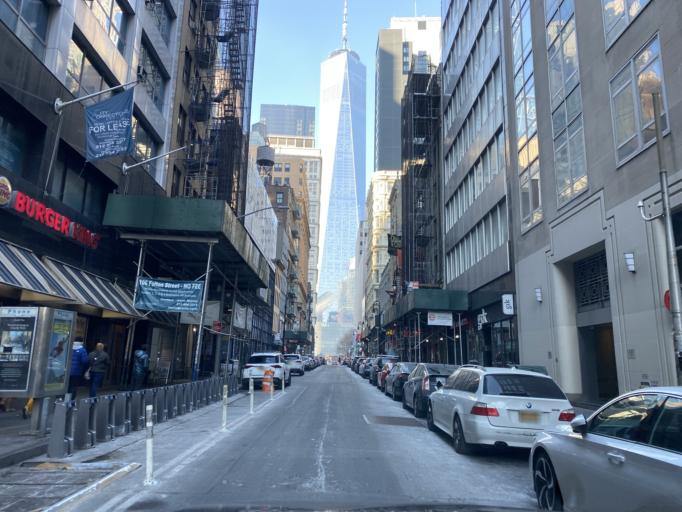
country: US
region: New York
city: New York City
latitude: 40.7098
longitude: -74.0067
